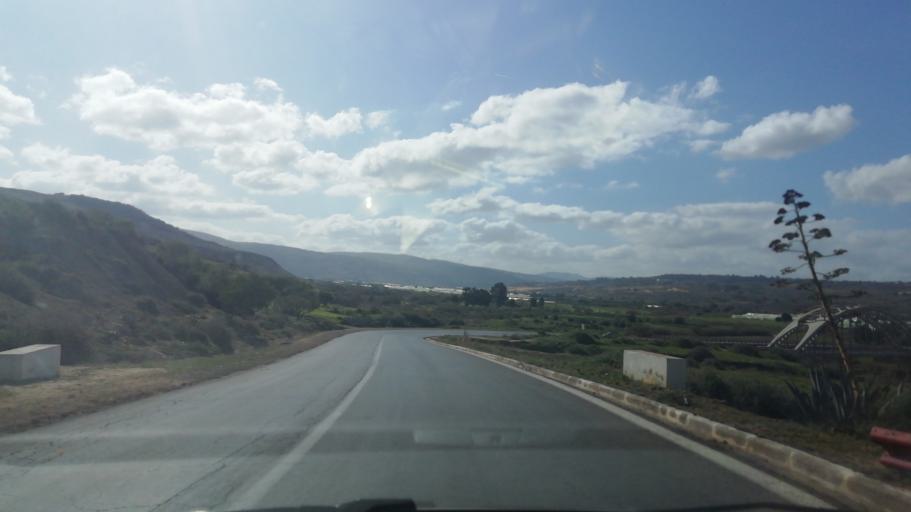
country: DZ
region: Relizane
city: Mazouna
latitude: 36.3058
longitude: 0.6711
